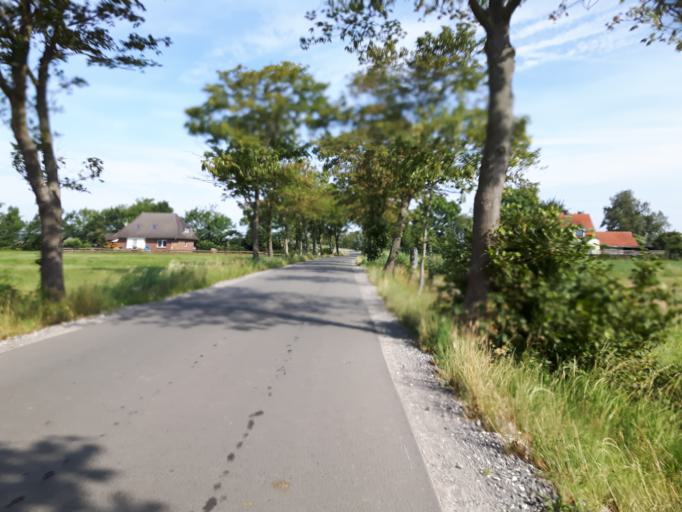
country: DE
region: Lower Saxony
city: Elsfleth
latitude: 53.1915
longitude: 8.4879
